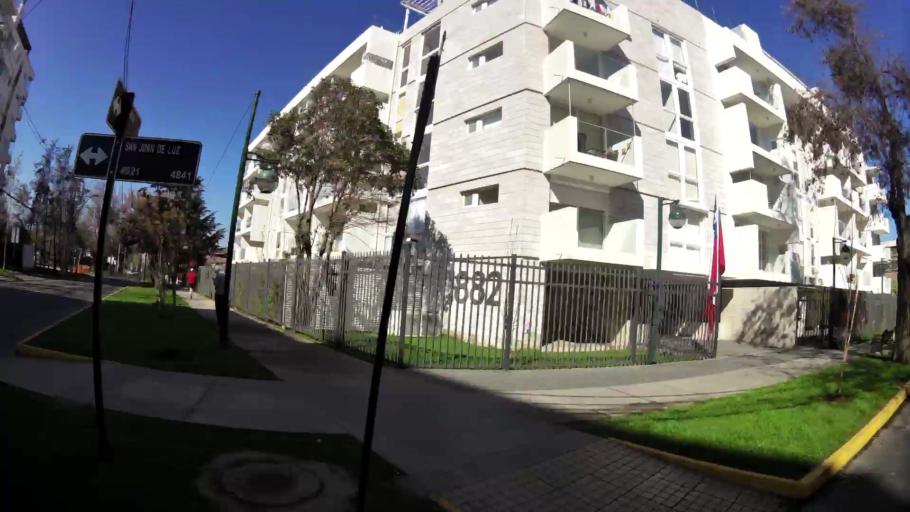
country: CL
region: Santiago Metropolitan
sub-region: Provincia de Santiago
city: Villa Presidente Frei, Nunoa, Santiago, Chile
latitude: -33.4370
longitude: -70.5783
